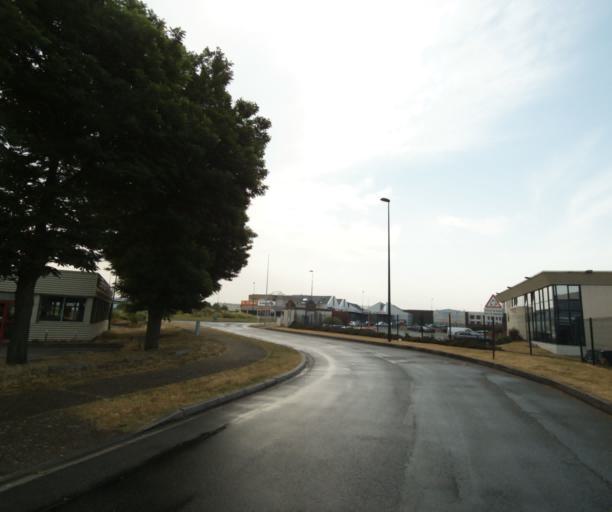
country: FR
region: Ile-de-France
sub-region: Departement du Val-d'Oise
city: Neuville-sur-Oise
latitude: 49.0061
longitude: 2.0768
